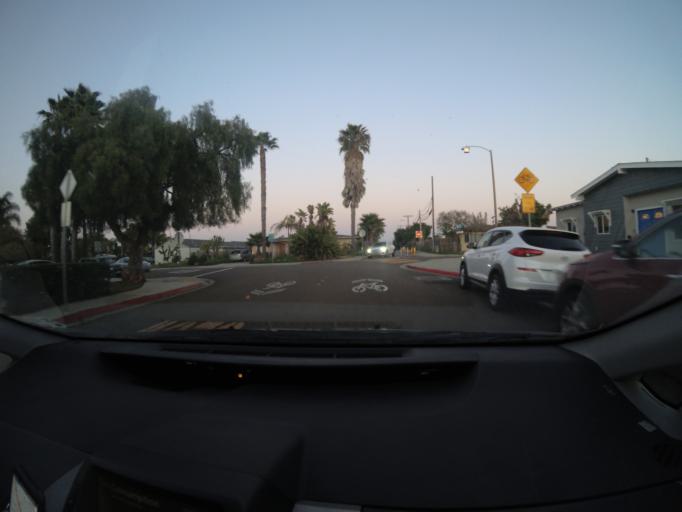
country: US
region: California
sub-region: San Diego County
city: Imperial Beach
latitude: 32.5802
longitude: -117.1184
